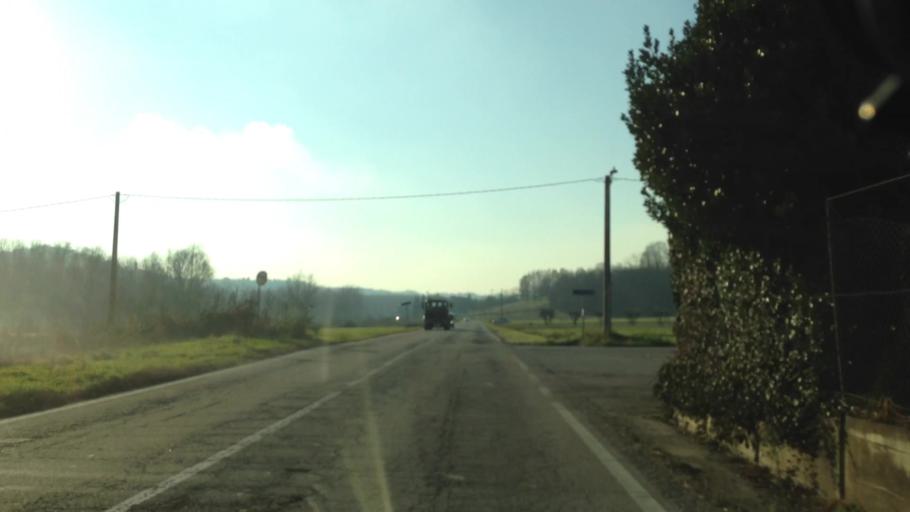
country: IT
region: Piedmont
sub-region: Provincia di Asti
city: Cortiglione
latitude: 44.8350
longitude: 8.3751
